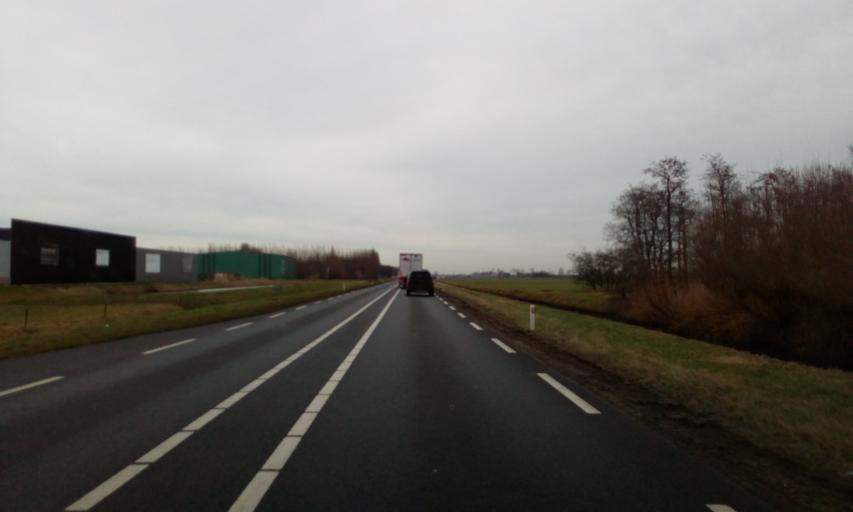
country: NL
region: Gelderland
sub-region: Gemeente Zaltbommel
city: Nederhemert-Noord
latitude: 51.7939
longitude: 5.1978
